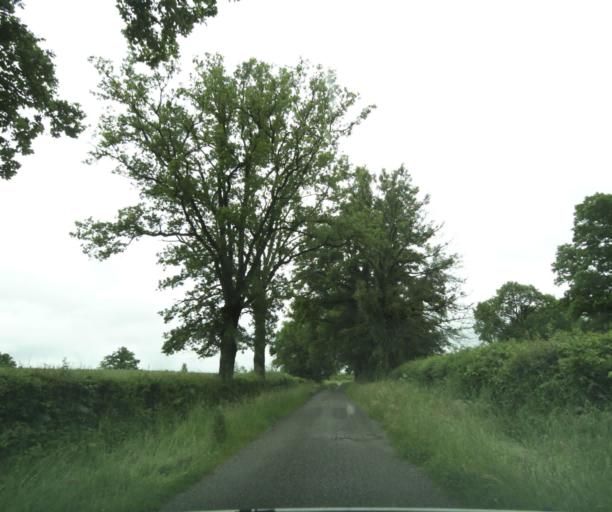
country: FR
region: Bourgogne
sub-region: Departement de Saone-et-Loire
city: Charolles
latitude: 46.4553
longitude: 4.3337
